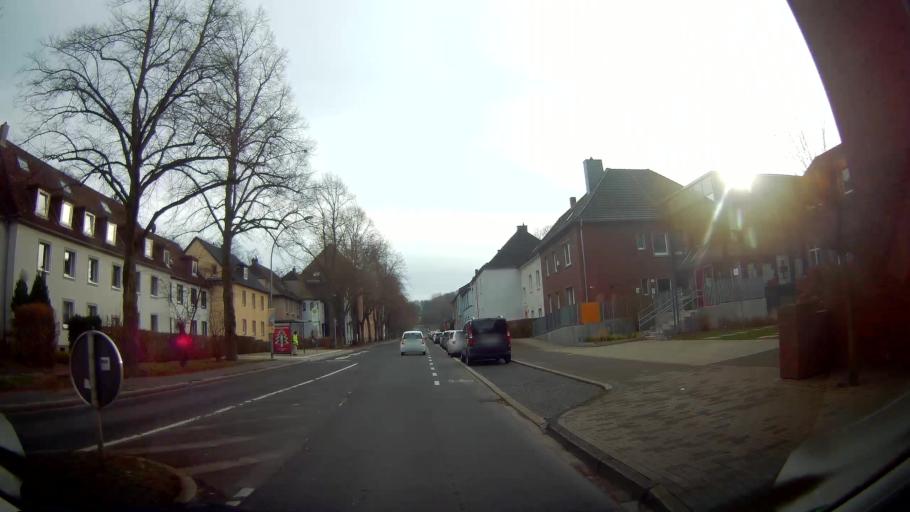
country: DE
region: North Rhine-Westphalia
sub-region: Regierungsbezirk Arnsberg
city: Herne
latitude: 51.5295
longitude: 7.2404
